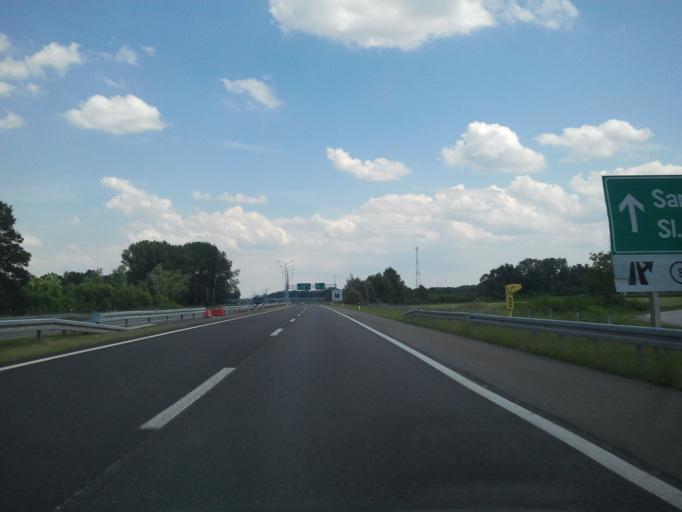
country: HR
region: Brodsko-Posavska
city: Garcin
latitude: 45.1451
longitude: 18.2959
